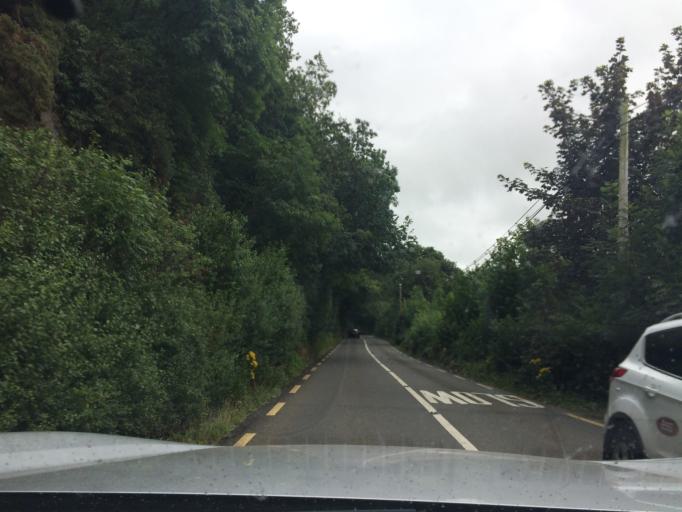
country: IE
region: Munster
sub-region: South Tipperary
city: Cluain Meala
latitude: 52.3095
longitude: -7.7897
